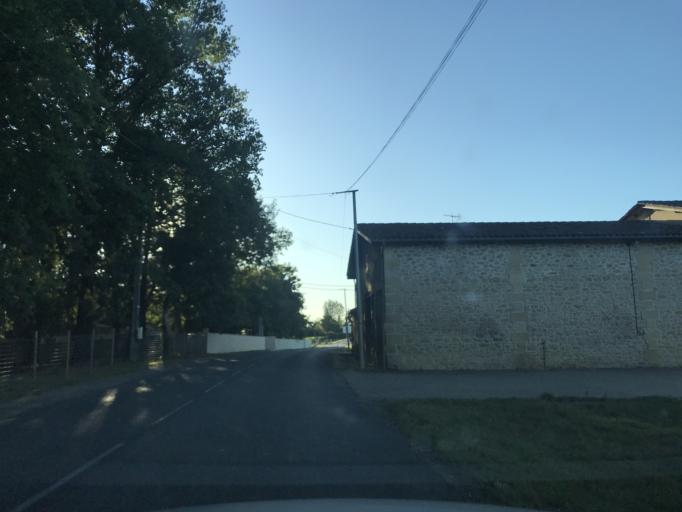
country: FR
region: Aquitaine
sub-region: Departement de la Gironde
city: Mouliets-et-Villemartin
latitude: 44.8943
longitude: -0.0523
